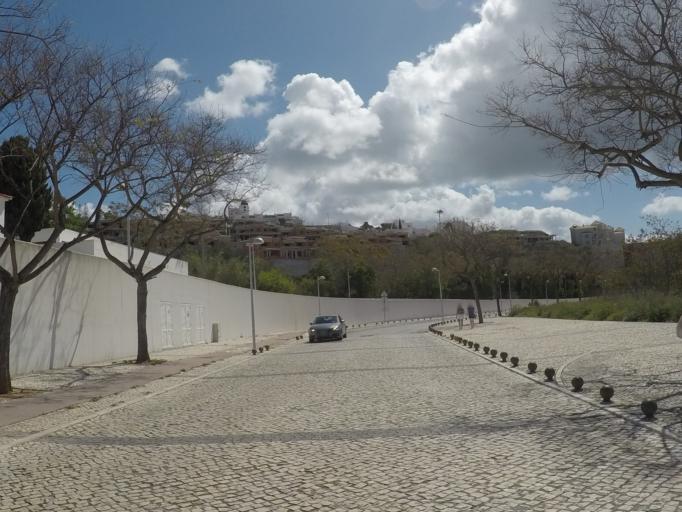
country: PT
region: Faro
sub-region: Albufeira
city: Albufeira
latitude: 37.0852
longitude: -8.2645
